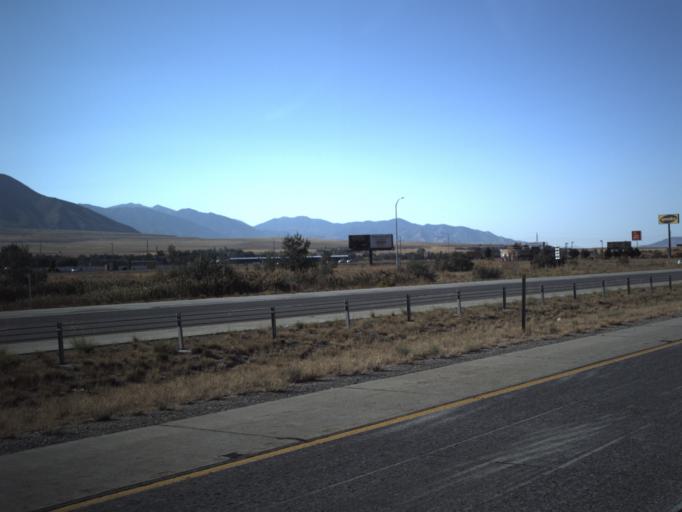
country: US
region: Utah
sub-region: Tooele County
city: Stansbury park
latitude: 40.6874
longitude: -112.2698
